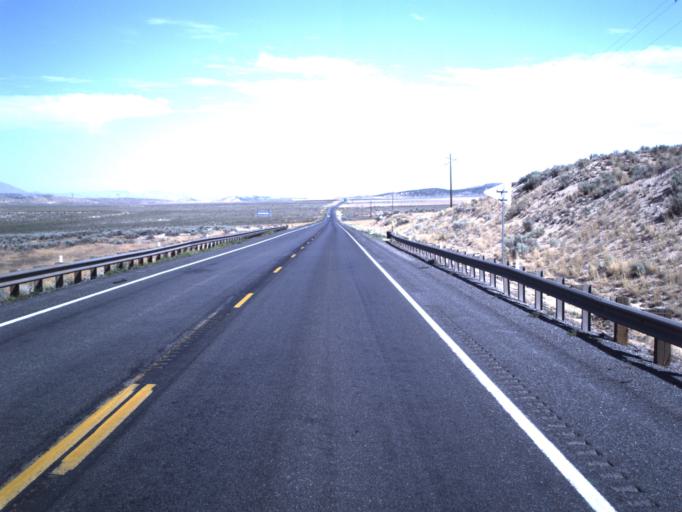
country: US
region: Utah
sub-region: Sanpete County
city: Gunnison
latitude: 39.2848
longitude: -111.8823
